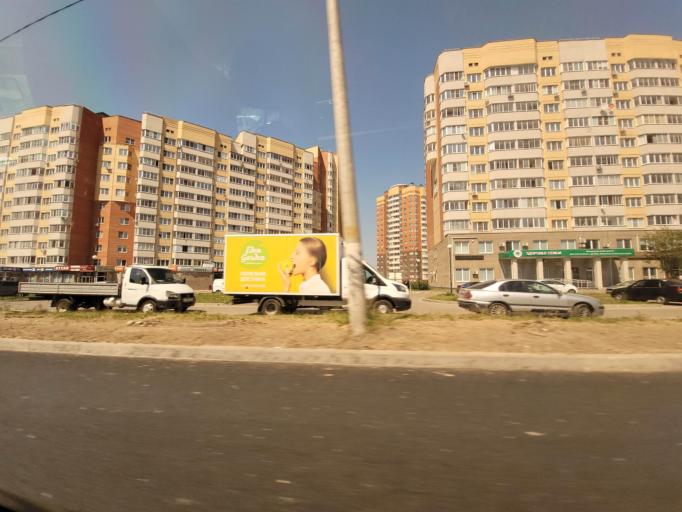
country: RU
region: Kaluga
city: Obninsk
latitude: 55.1229
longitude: 36.6087
